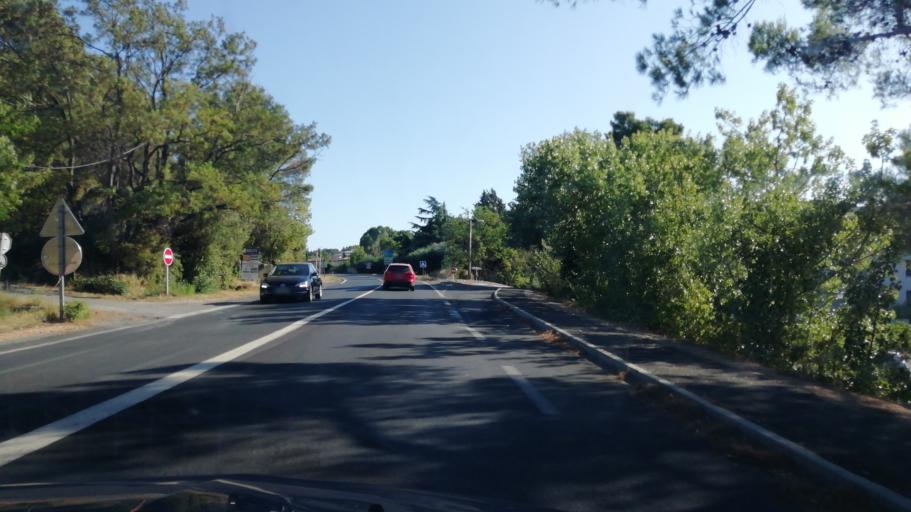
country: FR
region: Languedoc-Roussillon
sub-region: Departement de l'Herault
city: Nebian
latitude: 43.6294
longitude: 3.4382
